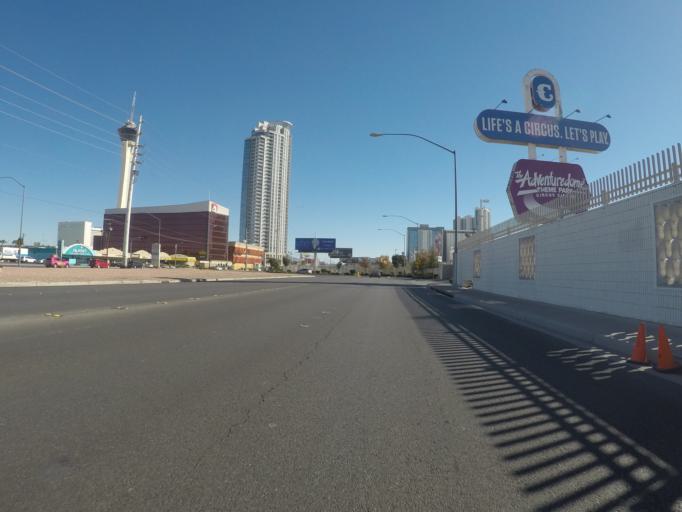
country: US
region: Nevada
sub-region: Clark County
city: Las Vegas
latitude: 36.1433
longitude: -115.1631
